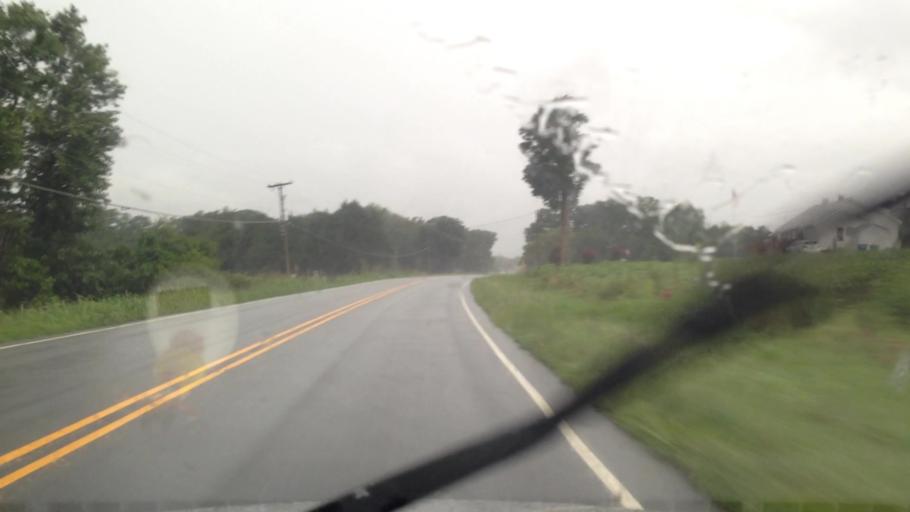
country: US
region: North Carolina
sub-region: Rockingham County
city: Reidsville
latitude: 36.2888
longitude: -79.7391
